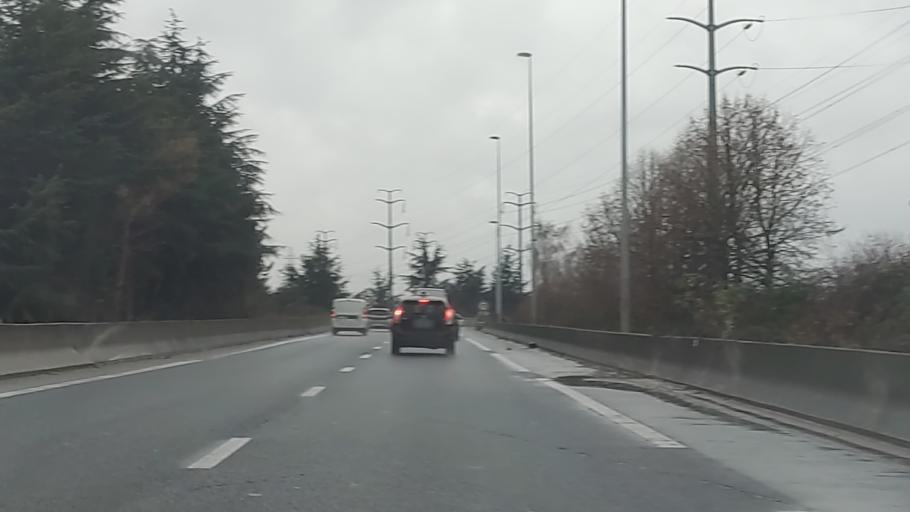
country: FR
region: Ile-de-France
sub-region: Departement du Val-de-Marne
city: Bonneuil-sur-Marne
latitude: 48.7574
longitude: 2.4751
